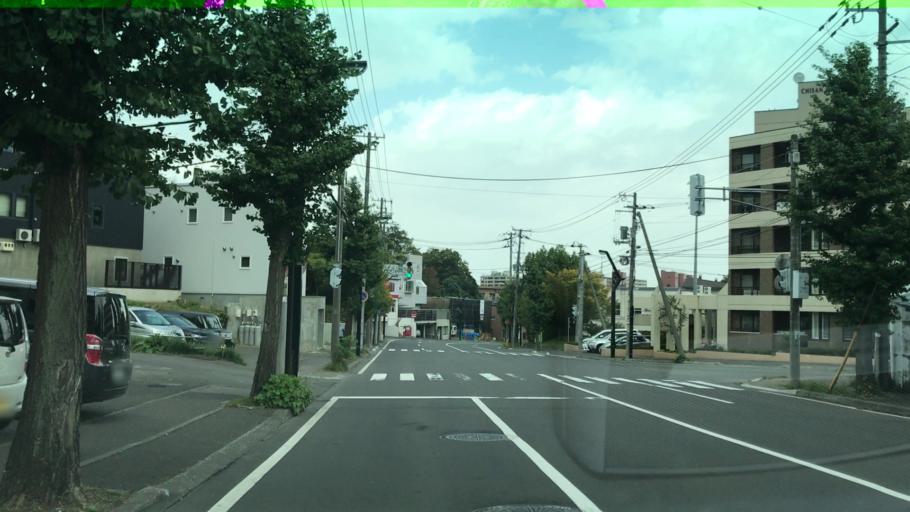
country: JP
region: Hokkaido
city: Sapporo
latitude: 43.0434
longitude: 141.3193
